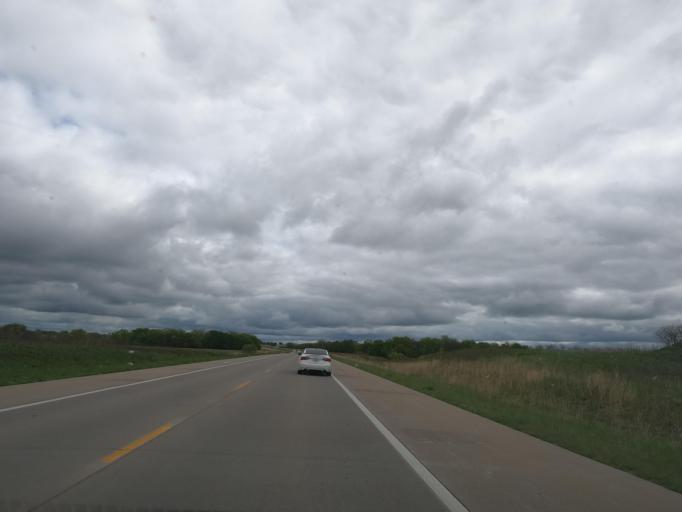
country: US
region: Kansas
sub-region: Wilson County
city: Neodesha
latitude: 37.3501
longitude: -95.6144
